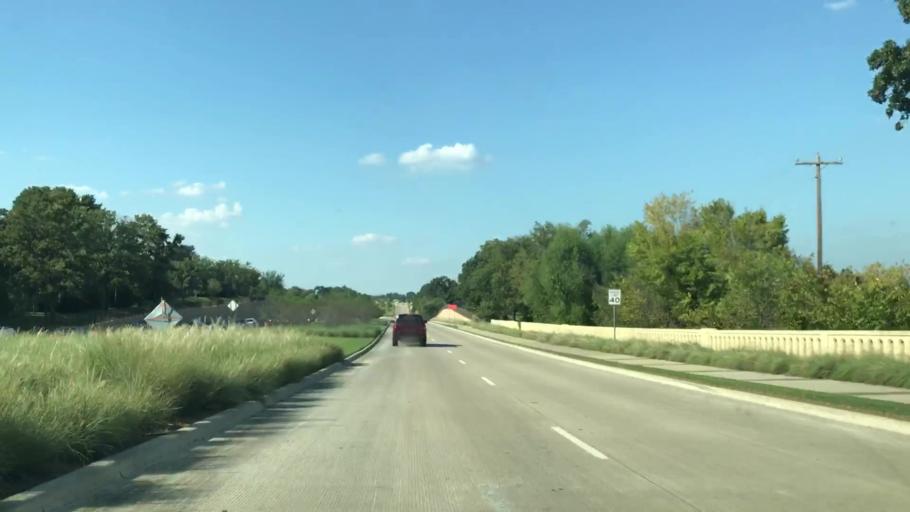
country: US
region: Texas
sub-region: Denton County
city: Trophy Club
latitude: 32.9610
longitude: -97.1858
